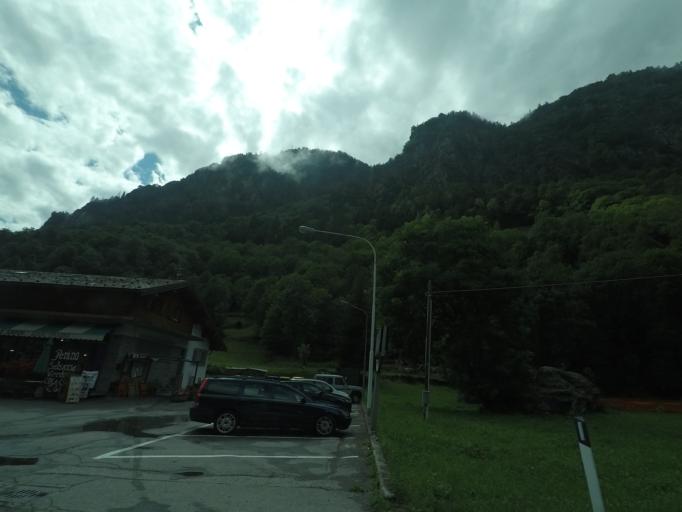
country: IT
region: Aosta Valley
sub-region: Valle d'Aosta
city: Antey-Saint-Andre
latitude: 45.8136
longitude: 7.5883
